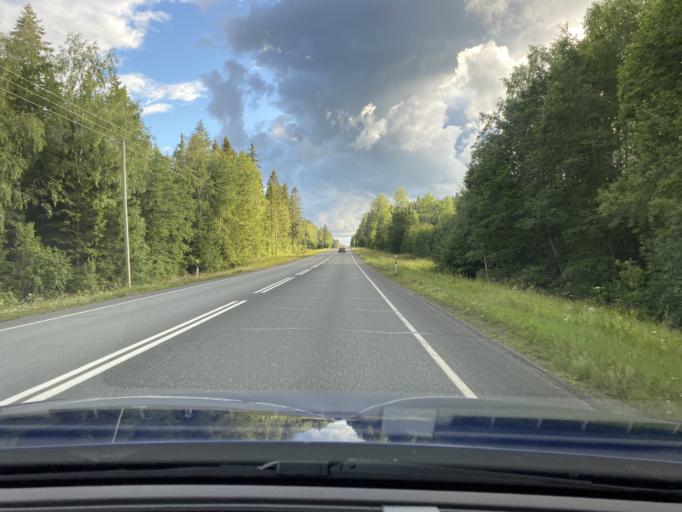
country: FI
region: Haeme
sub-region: Haemeenlinna
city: Renko
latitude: 60.8817
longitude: 24.2378
